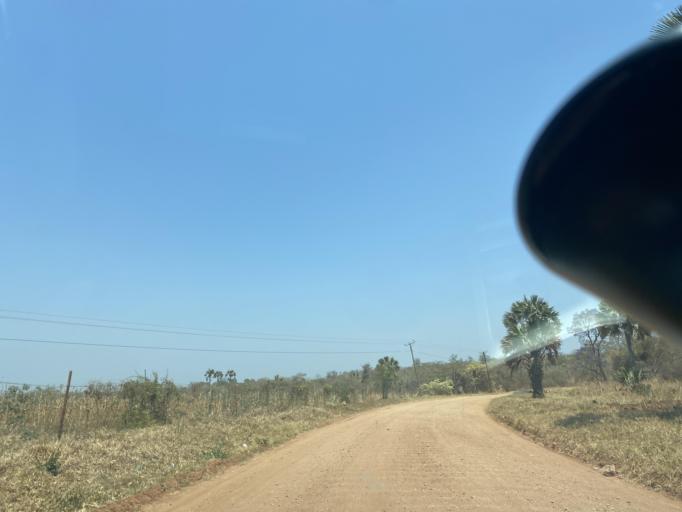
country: ZM
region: Lusaka
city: Kafue
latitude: -15.5492
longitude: 28.0665
